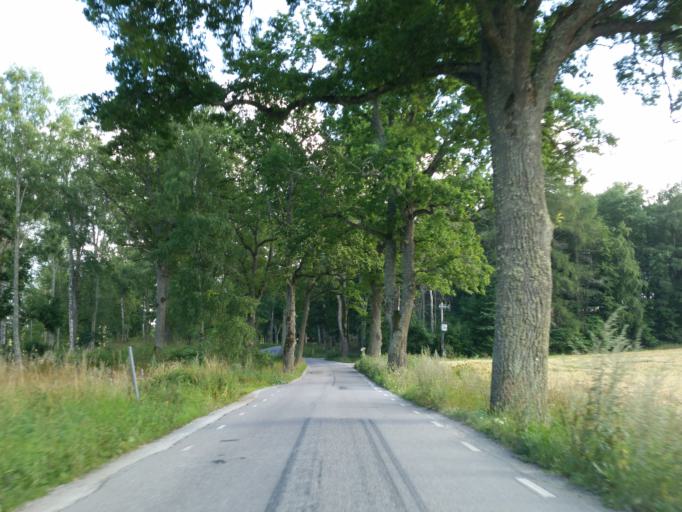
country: SE
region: Soedermanland
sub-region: Strangnas Kommun
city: Mariefred
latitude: 59.2364
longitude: 17.3031
